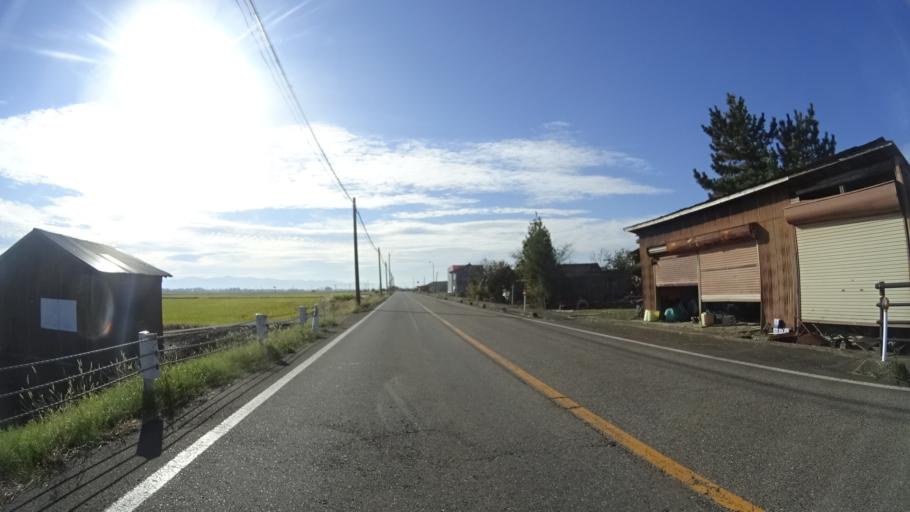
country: JP
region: Niigata
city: Mitsuke
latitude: 37.5731
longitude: 138.8415
